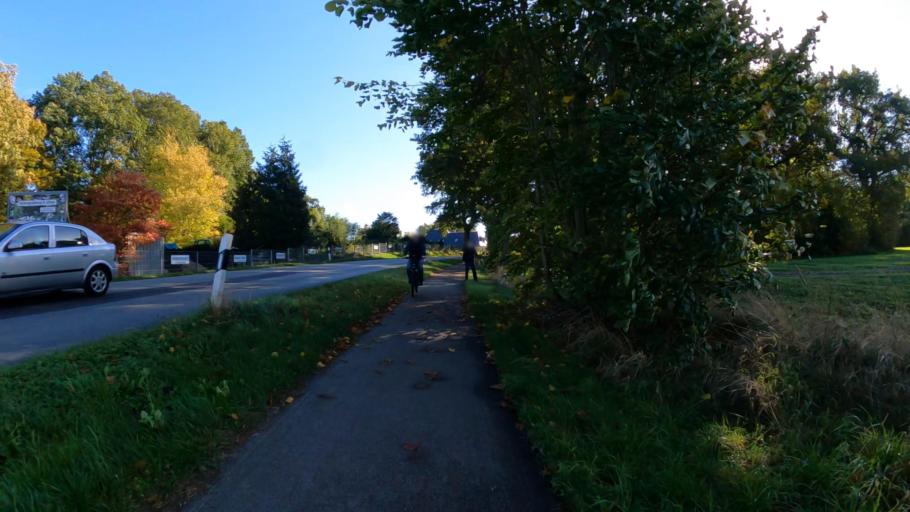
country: DE
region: Schleswig-Holstein
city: Ahrensburg
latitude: 53.6908
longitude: 10.2234
